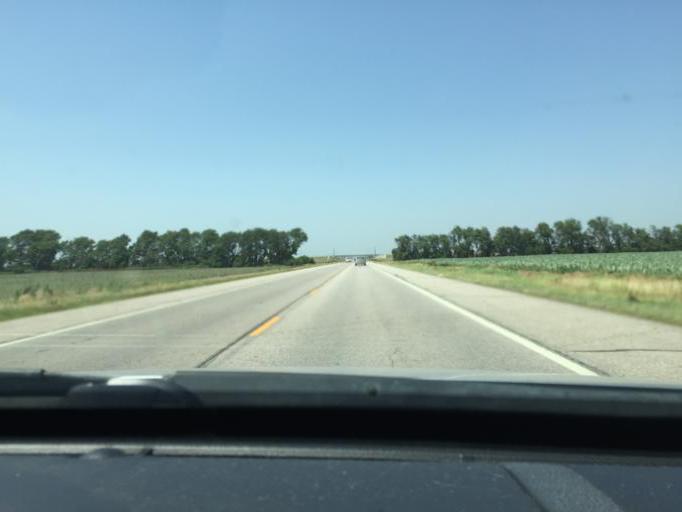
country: US
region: Kansas
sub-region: Reno County
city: South Hutchinson
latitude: 38.0190
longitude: -97.8669
